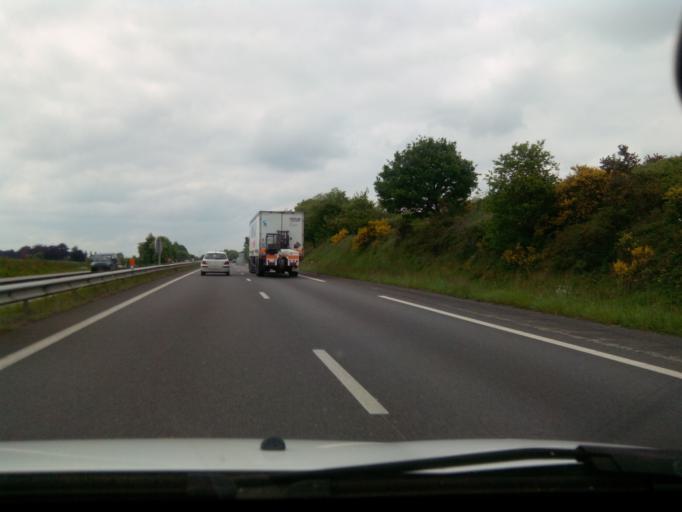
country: FR
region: Brittany
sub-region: Departement des Cotes-d'Armor
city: Broons
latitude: 48.3047
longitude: -2.2351
